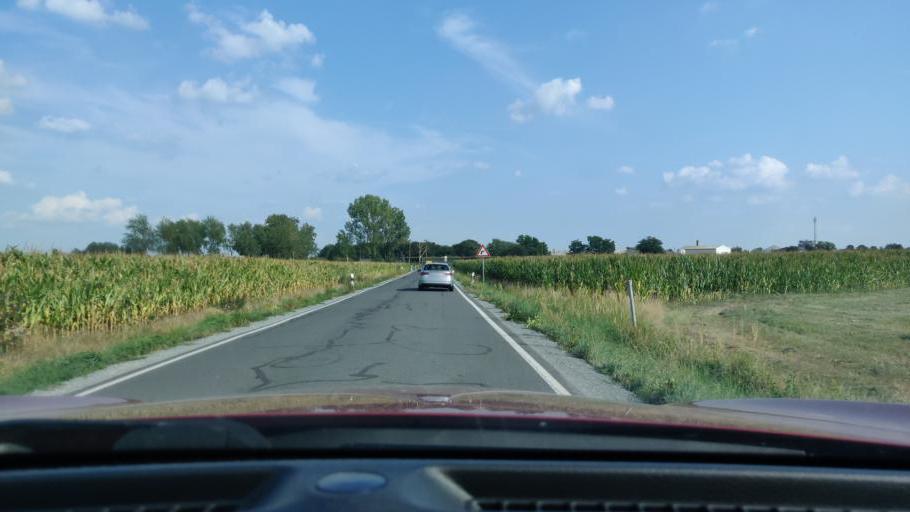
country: DE
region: Saxony
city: Mockrehna
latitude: 51.4888
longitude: 12.8641
